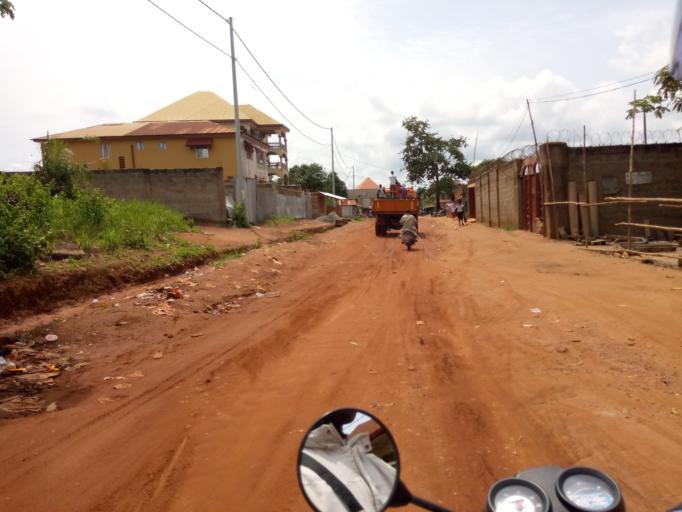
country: SL
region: Western Area
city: Waterloo
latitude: 8.3591
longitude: -13.0784
